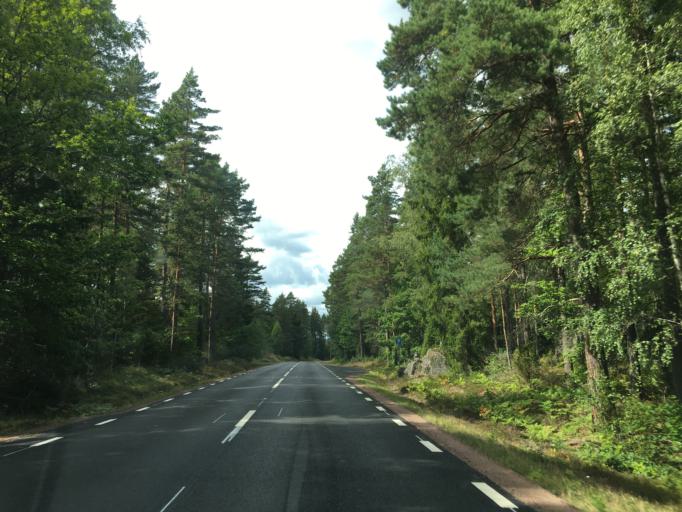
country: SE
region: Kalmar
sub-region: Nybro Kommun
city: Nybro
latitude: 56.9149
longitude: 16.0009
